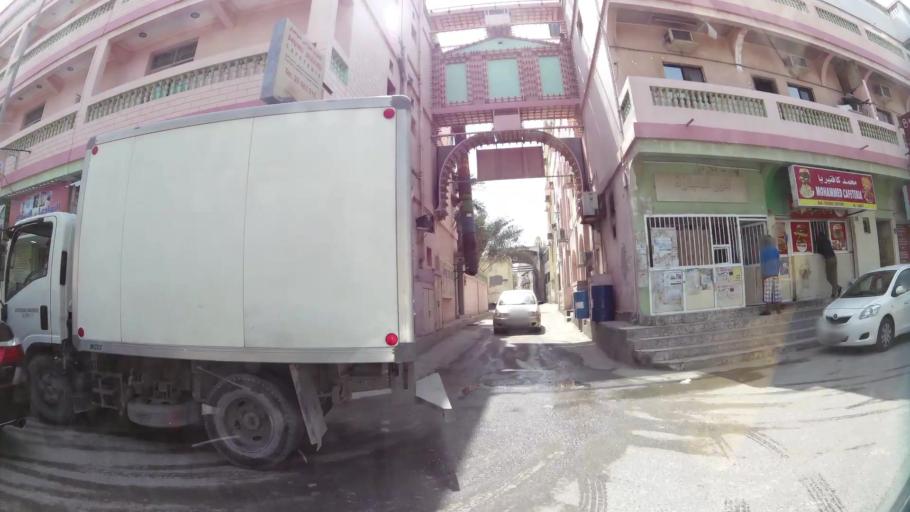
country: BH
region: Manama
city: Jidd Hafs
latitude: 26.2312
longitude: 50.4939
